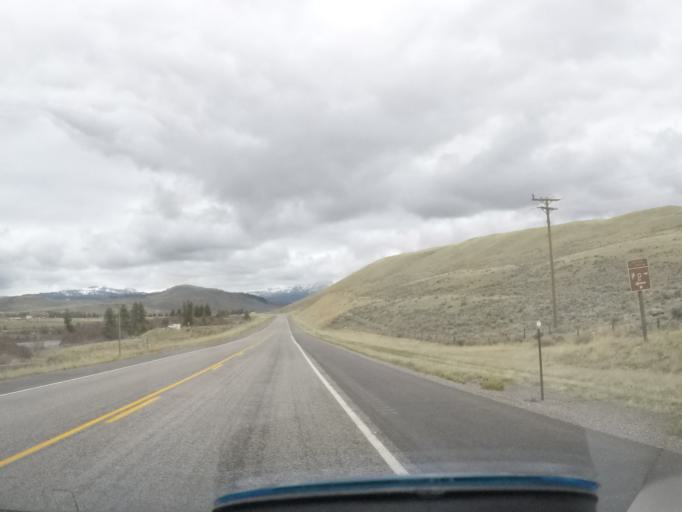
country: US
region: Wyoming
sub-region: Sublette County
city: Pinedale
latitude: 43.5901
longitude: -109.7731
